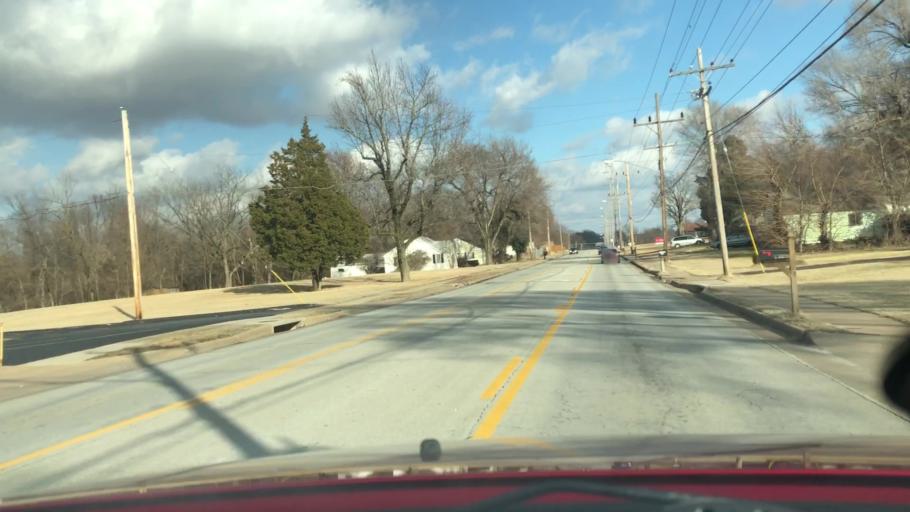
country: US
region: Missouri
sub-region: Greene County
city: Springfield
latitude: 37.2515
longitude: -93.2860
